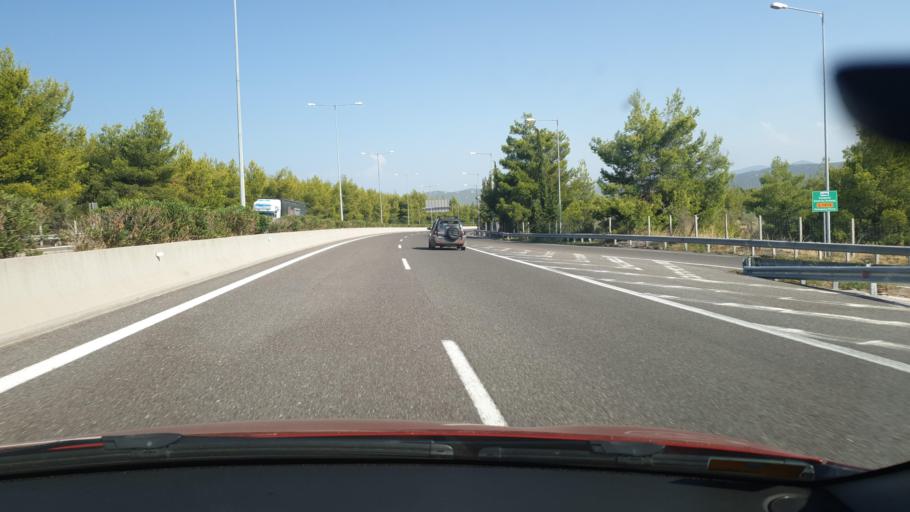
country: GR
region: Central Greece
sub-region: Nomos Fthiotidos
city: Martinon
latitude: 38.5955
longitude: 23.1930
